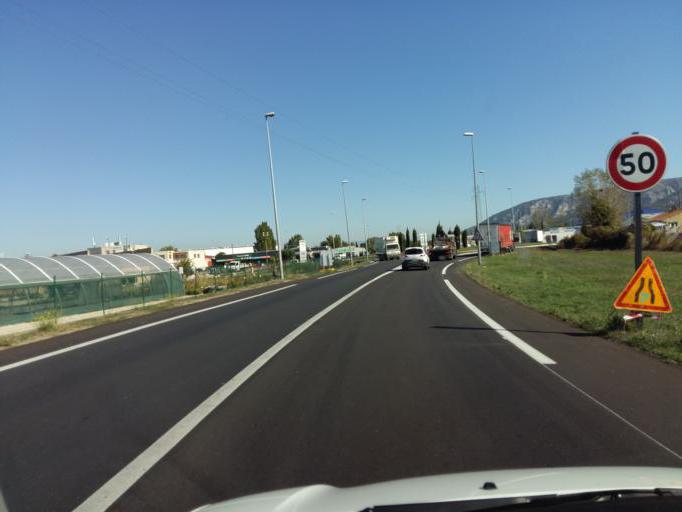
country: FR
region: Provence-Alpes-Cote d'Azur
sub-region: Departement du Vaucluse
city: Cavaillon
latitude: 43.8251
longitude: 5.0579
